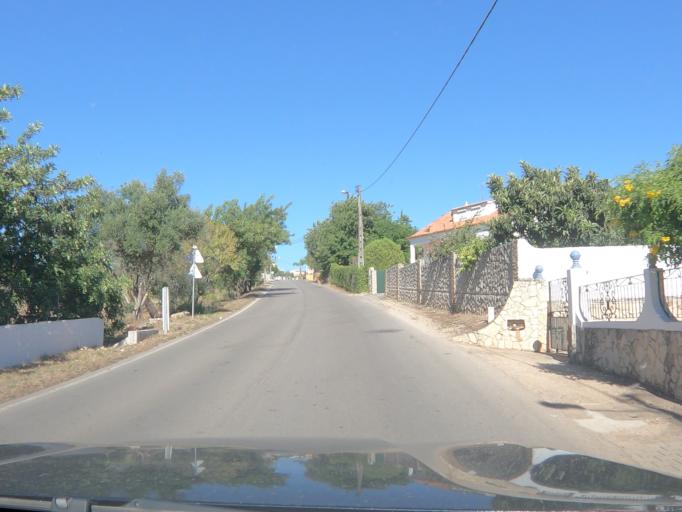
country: PT
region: Faro
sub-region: Loule
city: Almancil
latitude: 37.1084
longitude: -8.0382
